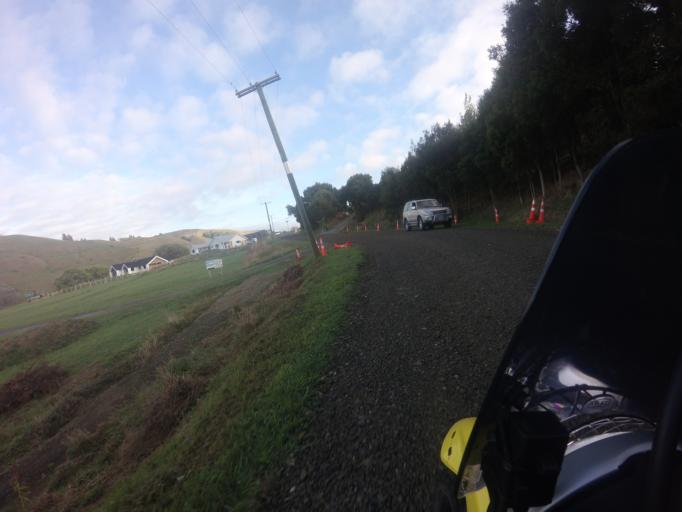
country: NZ
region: Gisborne
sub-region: Gisborne District
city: Gisborne
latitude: -38.6647
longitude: 178.0816
